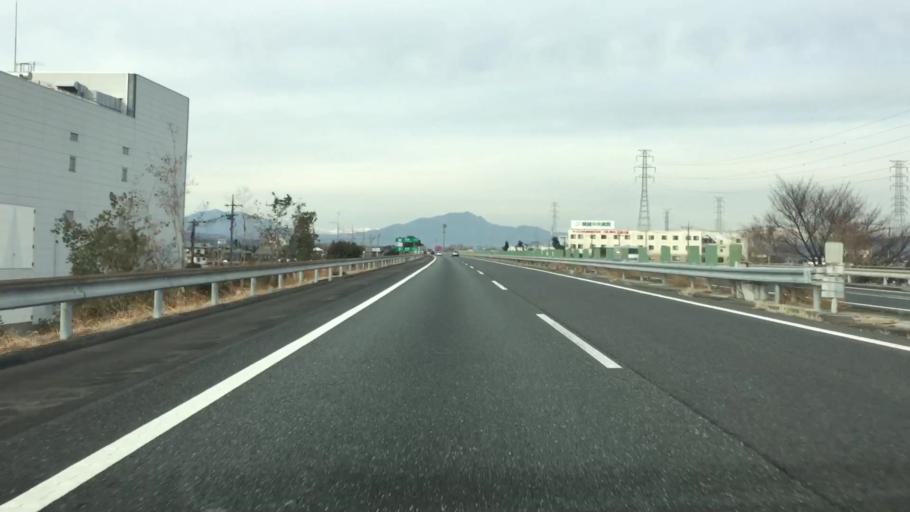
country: JP
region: Gunma
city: Kanekomachi
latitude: 36.4014
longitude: 139.0244
